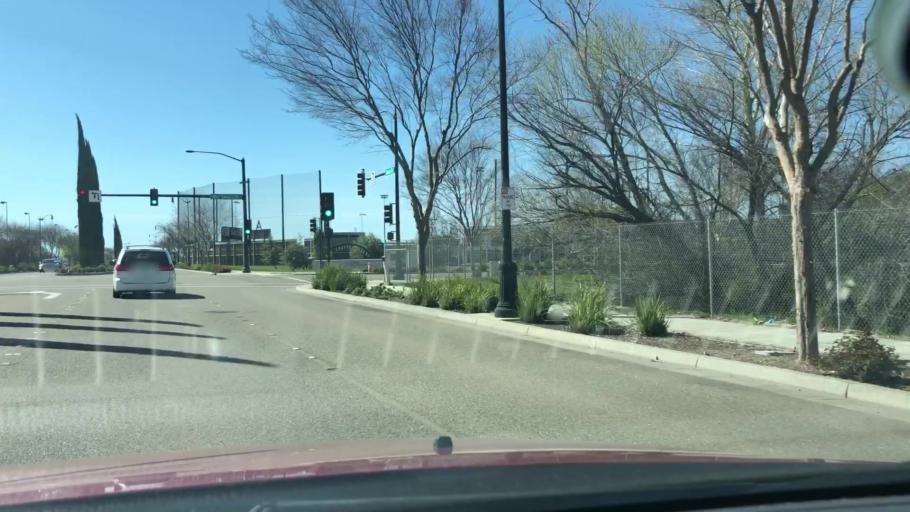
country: US
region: California
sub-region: San Joaquin County
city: Lathrop
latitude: 37.7864
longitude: -121.2564
